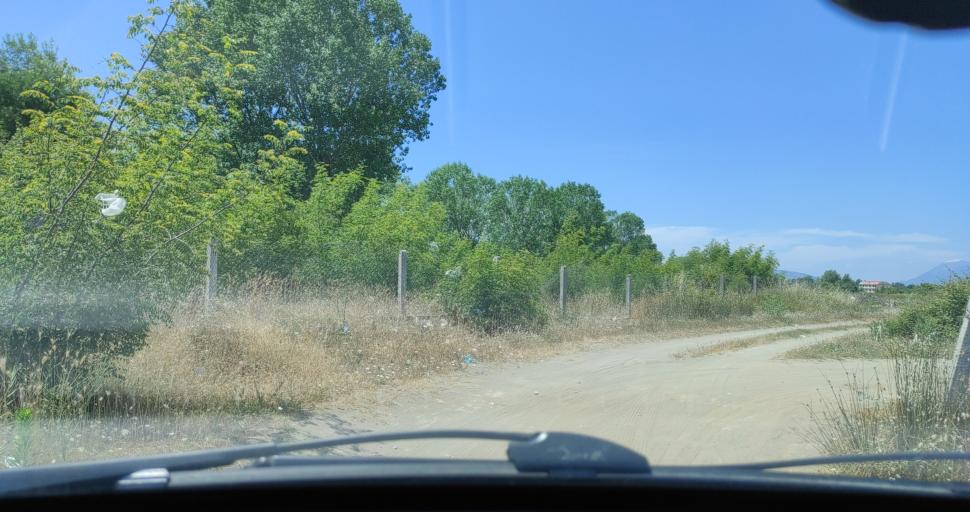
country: AL
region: Shkoder
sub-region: Rrethi i Shkodres
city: Velipoje
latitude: 41.8683
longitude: 19.3995
